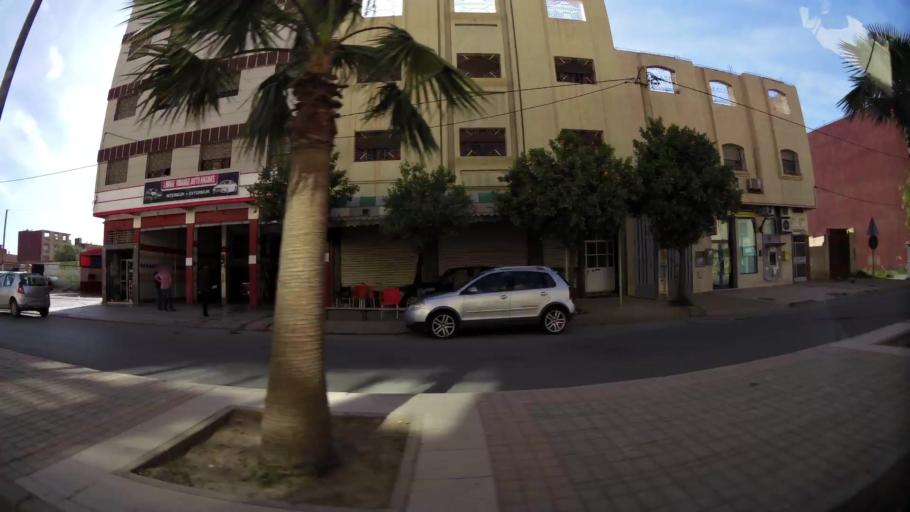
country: MA
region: Oriental
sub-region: Oujda-Angad
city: Oujda
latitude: 34.6721
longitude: -1.8936
